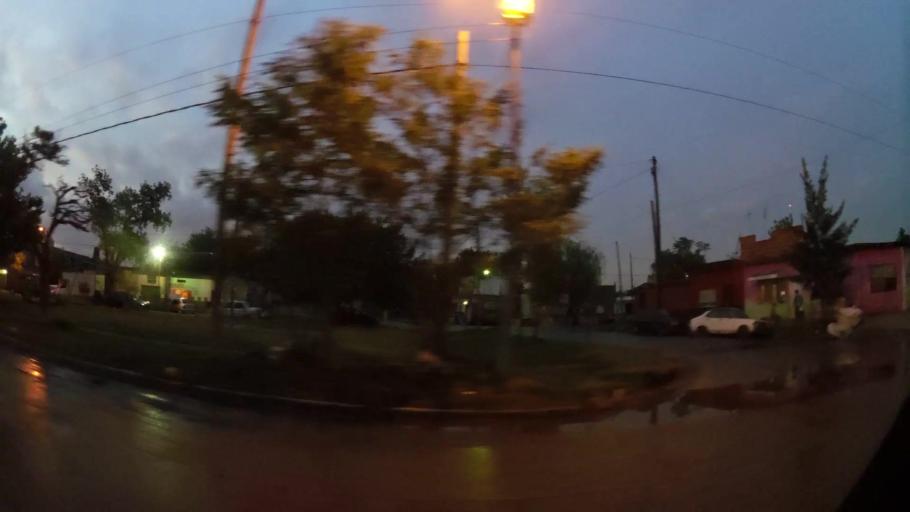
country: AR
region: Buenos Aires
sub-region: Partido de Lomas de Zamora
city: Lomas de Zamora
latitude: -34.7439
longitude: -58.3636
